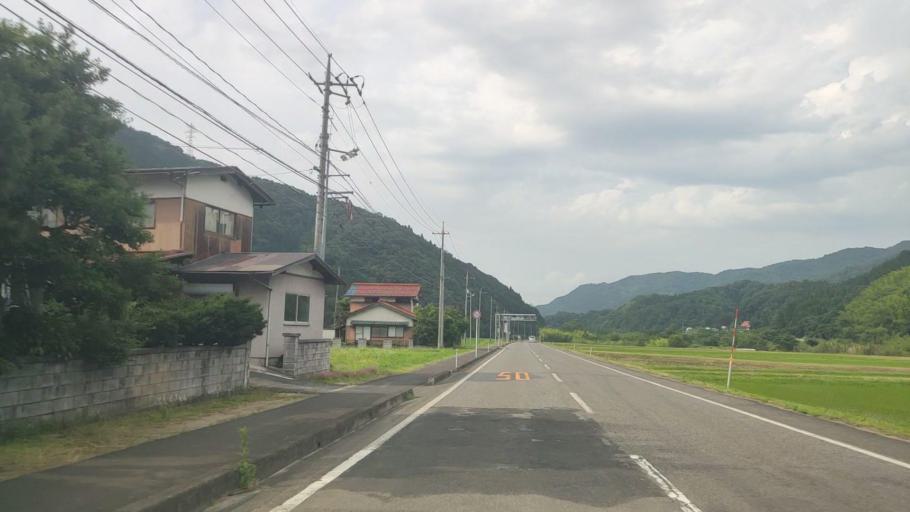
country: JP
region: Tottori
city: Kurayoshi
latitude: 35.3491
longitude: 133.8424
